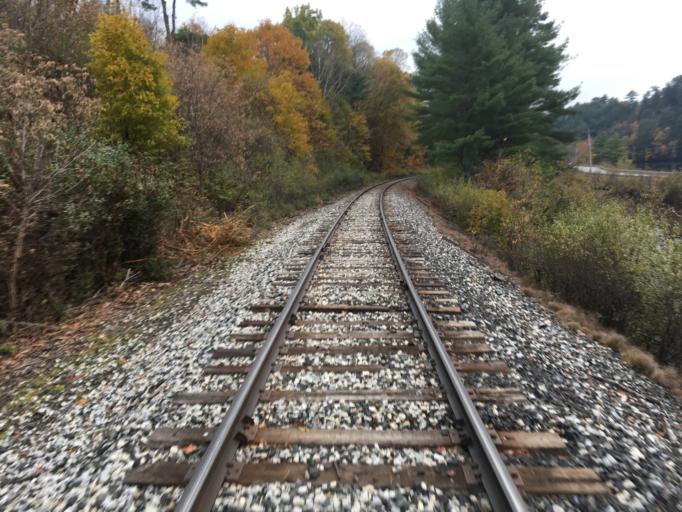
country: US
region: New Hampshire
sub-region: Grafton County
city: Hanover
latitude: 43.7074
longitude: -72.2998
